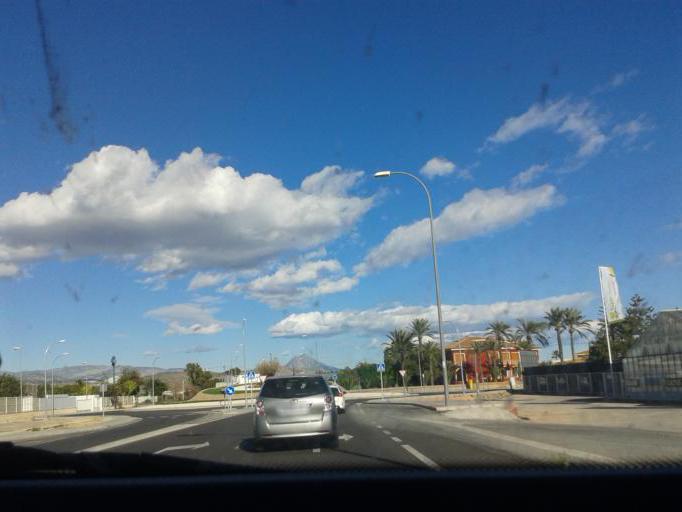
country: ES
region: Valencia
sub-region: Provincia de Alicante
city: el Campello
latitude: 38.4172
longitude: -0.4156
